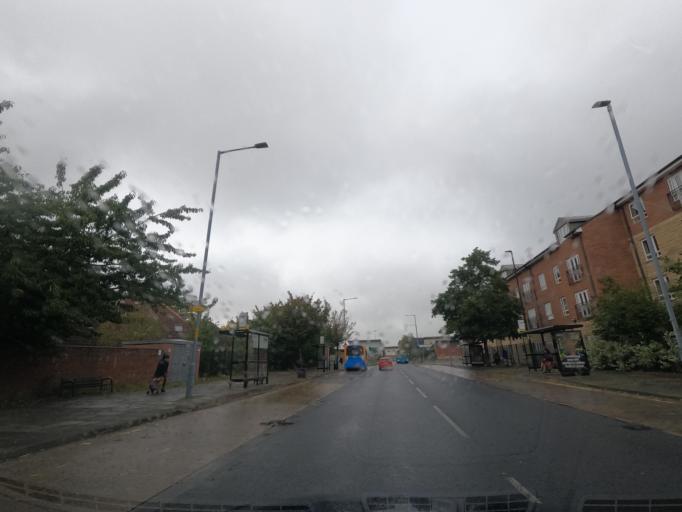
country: GB
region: England
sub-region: Middlesbrough
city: Middlesbrough
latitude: 54.5706
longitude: -1.2144
